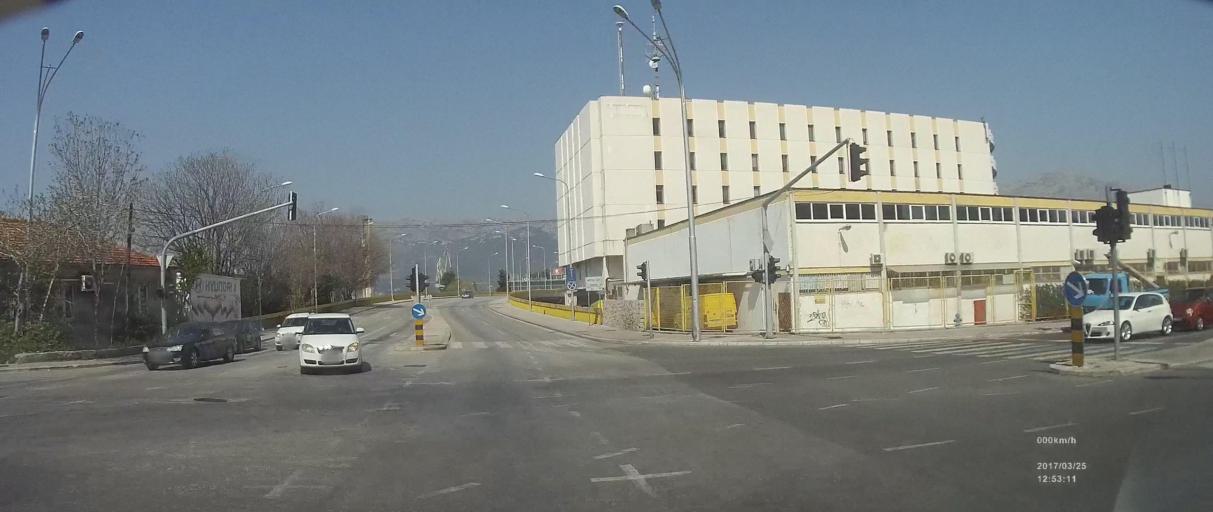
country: HR
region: Splitsko-Dalmatinska
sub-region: Grad Split
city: Split
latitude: 43.5206
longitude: 16.4490
